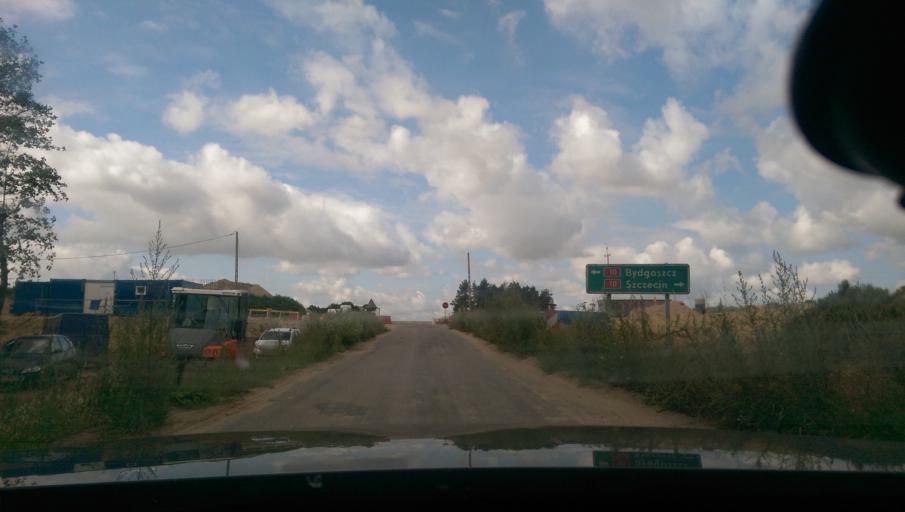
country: PL
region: Greater Poland Voivodeship
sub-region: Powiat pilski
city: Szydlowo
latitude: 53.2467
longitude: 16.6045
